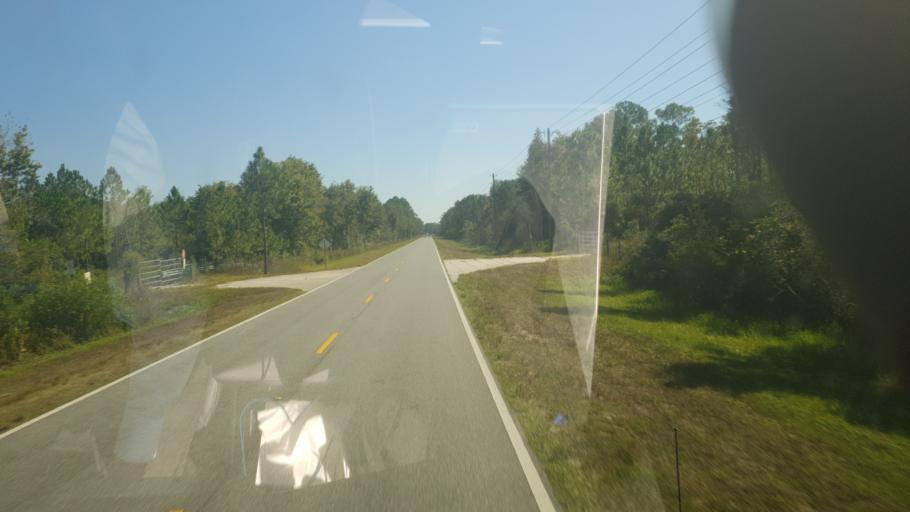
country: US
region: Florida
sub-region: Lake County
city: Four Corners
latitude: 28.3751
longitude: -81.7553
